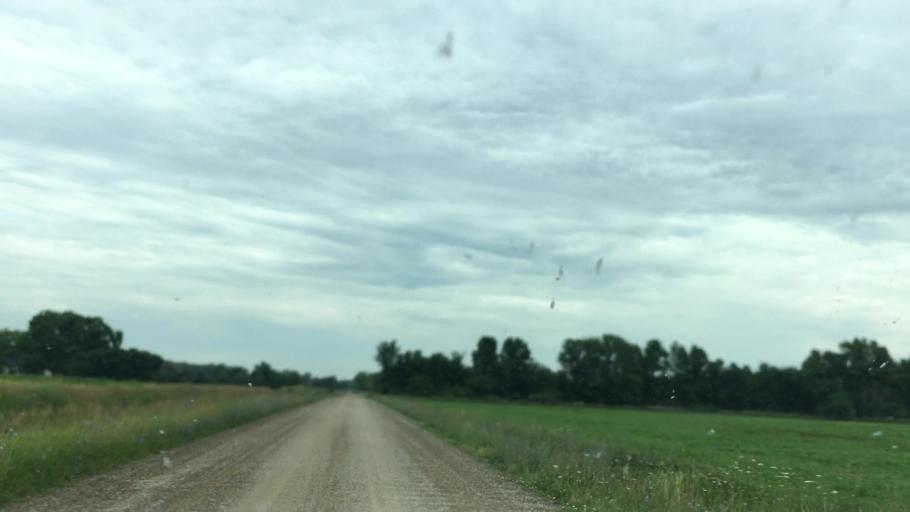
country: US
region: Michigan
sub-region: Clinton County
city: Saint Johns
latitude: 43.0798
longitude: -84.4839
